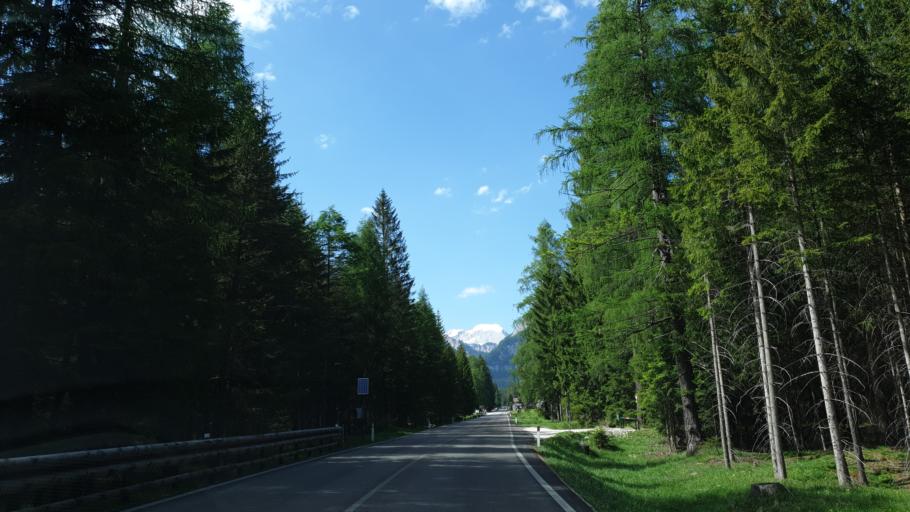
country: IT
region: Veneto
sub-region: Provincia di Belluno
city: Cortina d'Ampezzo
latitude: 46.5694
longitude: 12.1188
